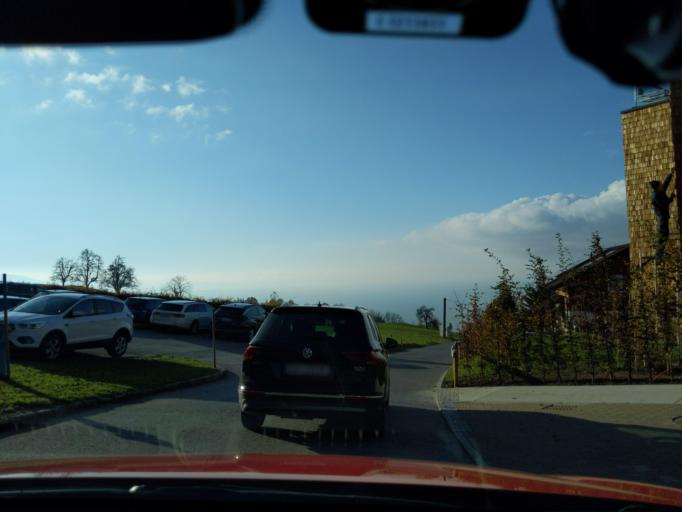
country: AT
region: Vorarlberg
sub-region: Politischer Bezirk Bregenz
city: Bregenz
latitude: 47.5151
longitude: 9.7676
